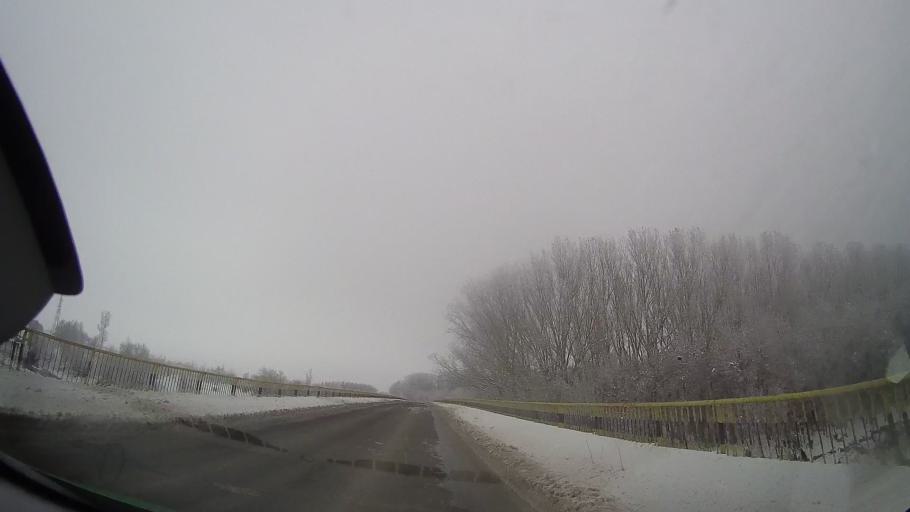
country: RO
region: Neamt
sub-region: Comuna Horia
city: Cotu Vames
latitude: 46.8827
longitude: 26.9709
